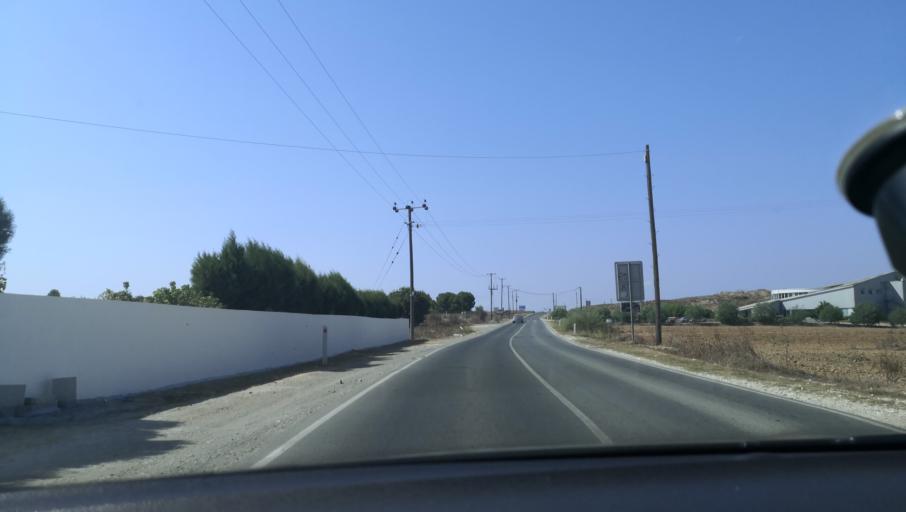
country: CY
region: Lefkosia
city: Kato Deftera
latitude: 35.1210
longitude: 33.2627
